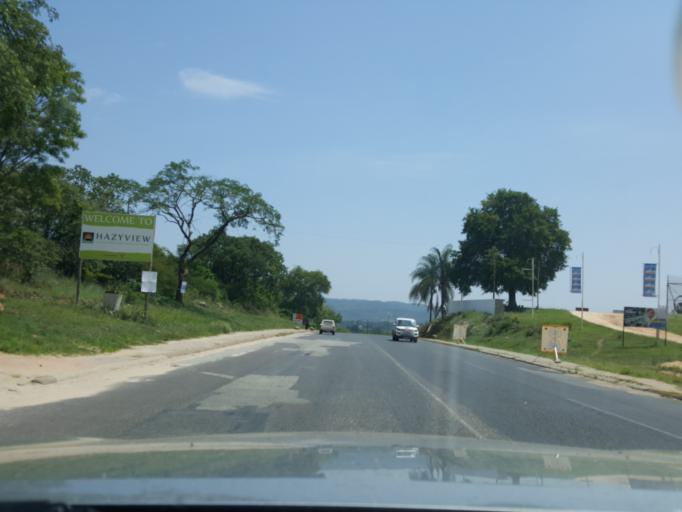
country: ZA
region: Mpumalanga
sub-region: Ehlanzeni District
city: White River
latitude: -25.0615
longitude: 31.1295
